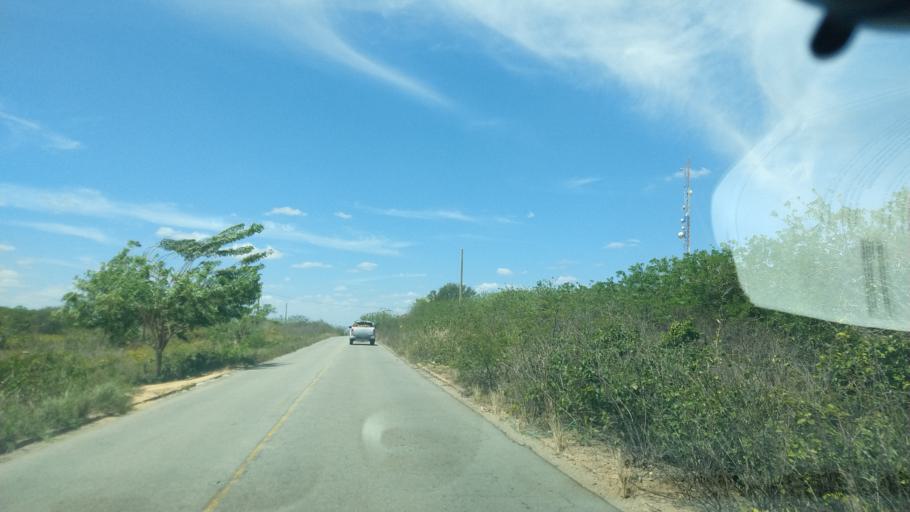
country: BR
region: Rio Grande do Norte
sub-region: Sao Paulo Do Potengi
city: Sao Paulo do Potengi
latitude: -5.9284
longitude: -35.5710
